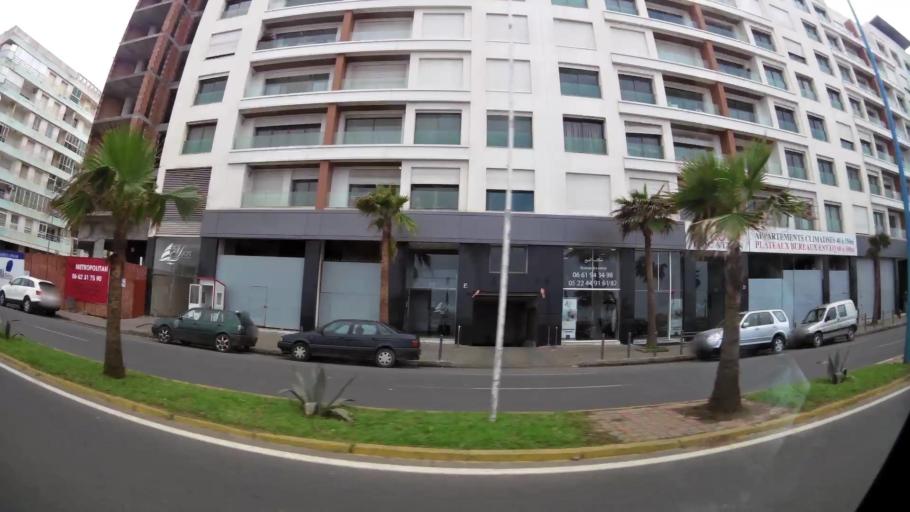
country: MA
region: Grand Casablanca
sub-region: Casablanca
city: Casablanca
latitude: 33.6042
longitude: -7.6454
